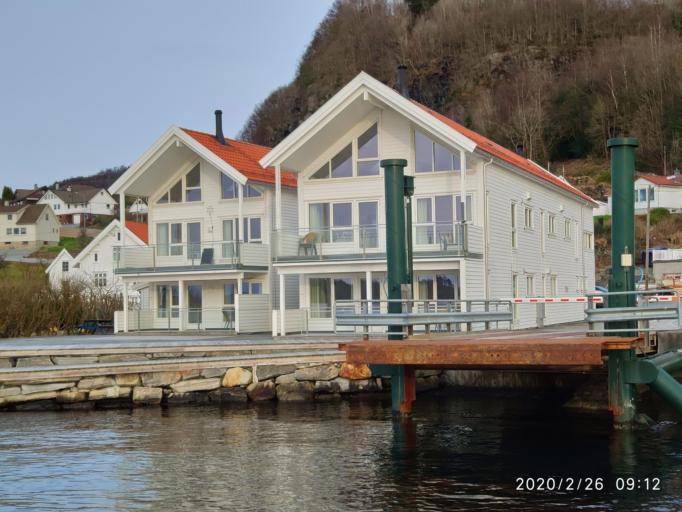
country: NO
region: Rogaland
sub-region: Finnoy
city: Judaberg
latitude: 59.3450
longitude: 5.8579
